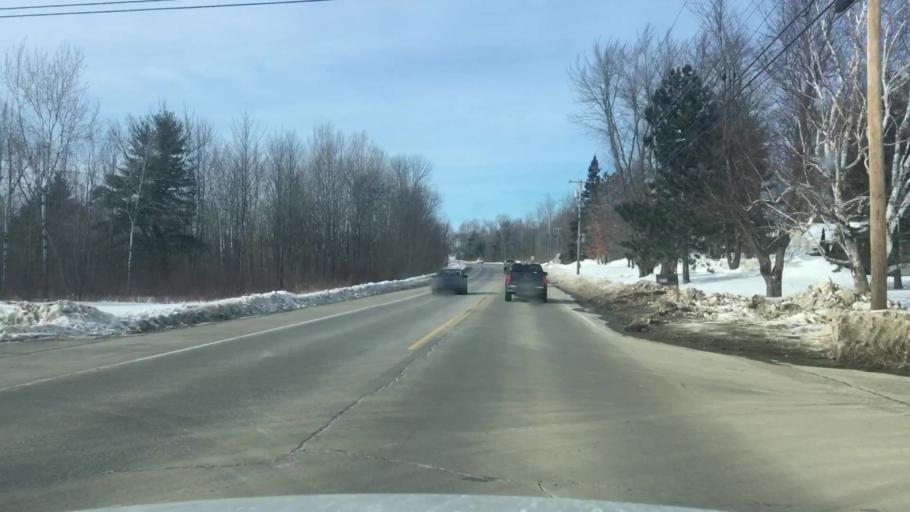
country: US
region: Maine
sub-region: Penobscot County
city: Kenduskeag
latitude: 44.9268
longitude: -68.9341
